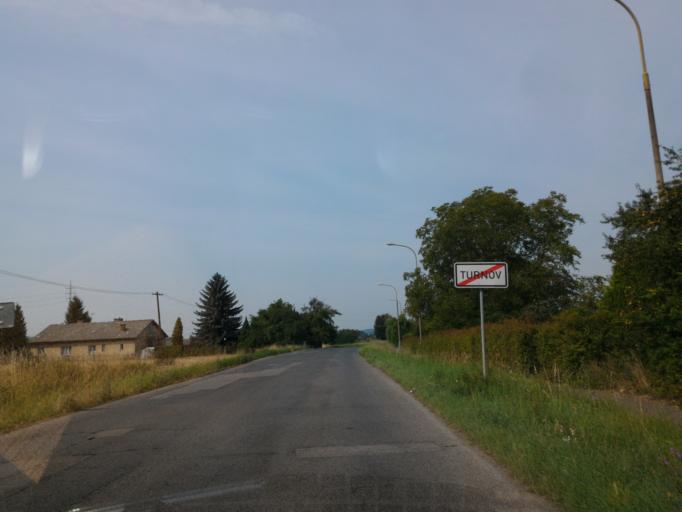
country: CZ
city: Ohrazenice
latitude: 50.5857
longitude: 15.1286
